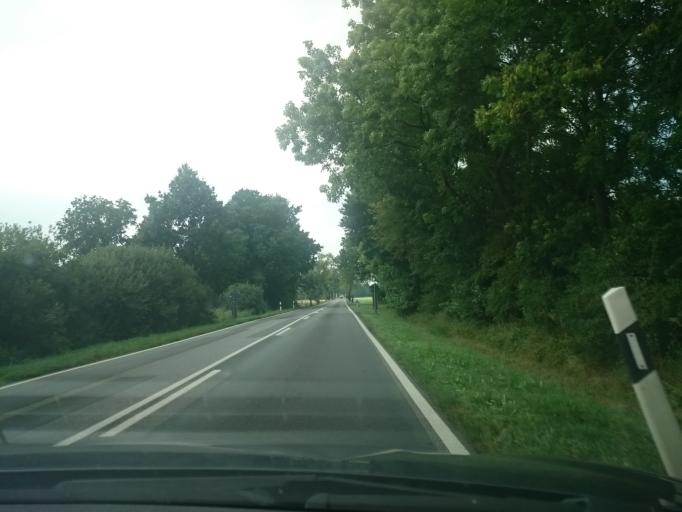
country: DE
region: Mecklenburg-Vorpommern
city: Ducherow
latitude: 53.7156
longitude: 13.8342
